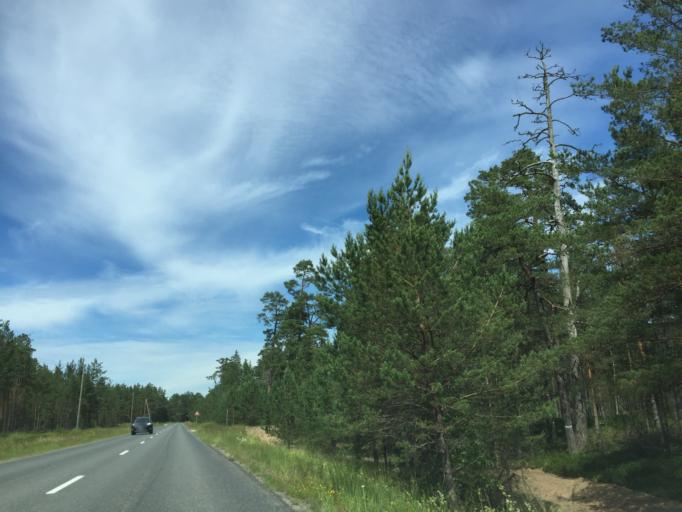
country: LV
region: Dundaga
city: Dundaga
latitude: 57.6455
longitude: 22.5715
